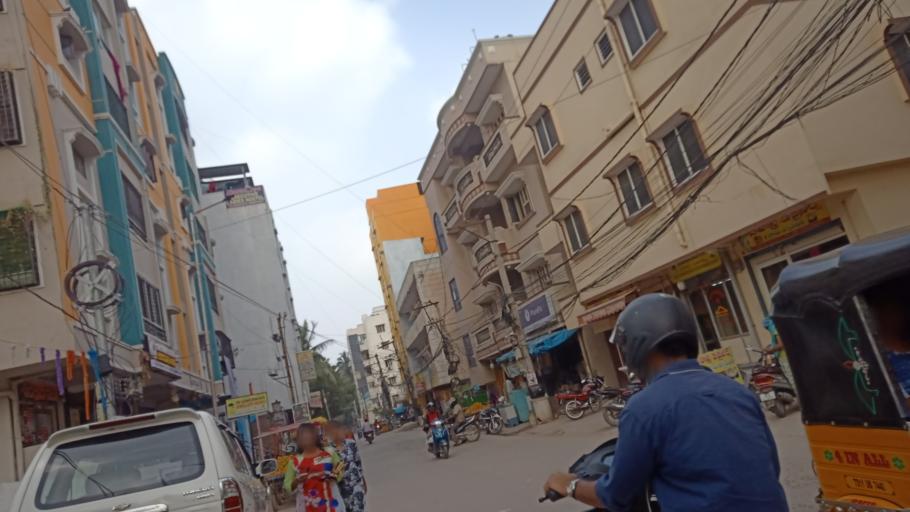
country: IN
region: Telangana
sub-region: Rangareddi
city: Kukatpalli
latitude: 17.4857
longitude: 78.4147
